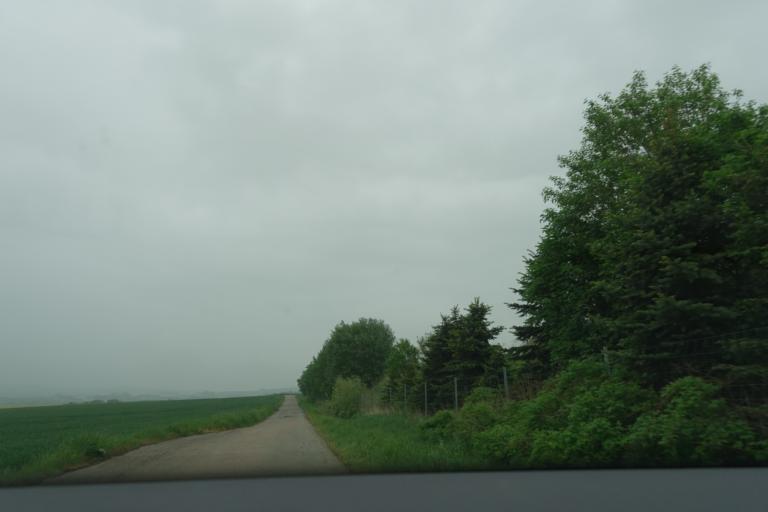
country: DE
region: Saxony
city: Eppendorf
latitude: 50.7786
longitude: 13.2413
